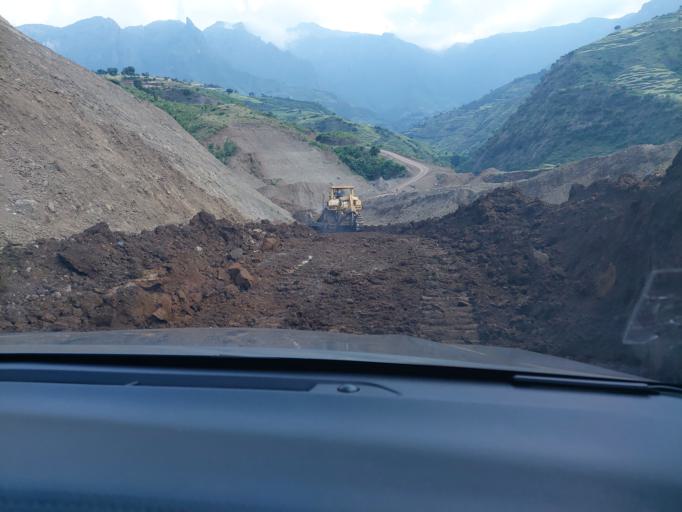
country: ET
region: Amhara
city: Debark'
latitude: 13.4023
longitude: 38.2158
